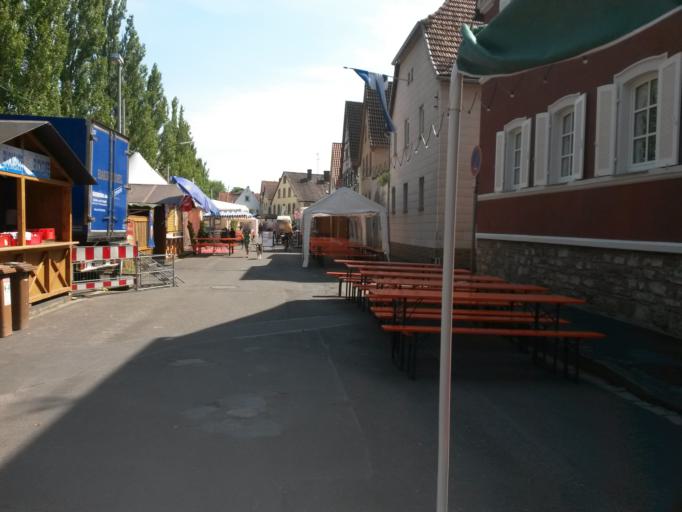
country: DE
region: Bavaria
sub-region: Regierungsbezirk Unterfranken
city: Margetshochheim
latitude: 49.8370
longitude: 9.8666
